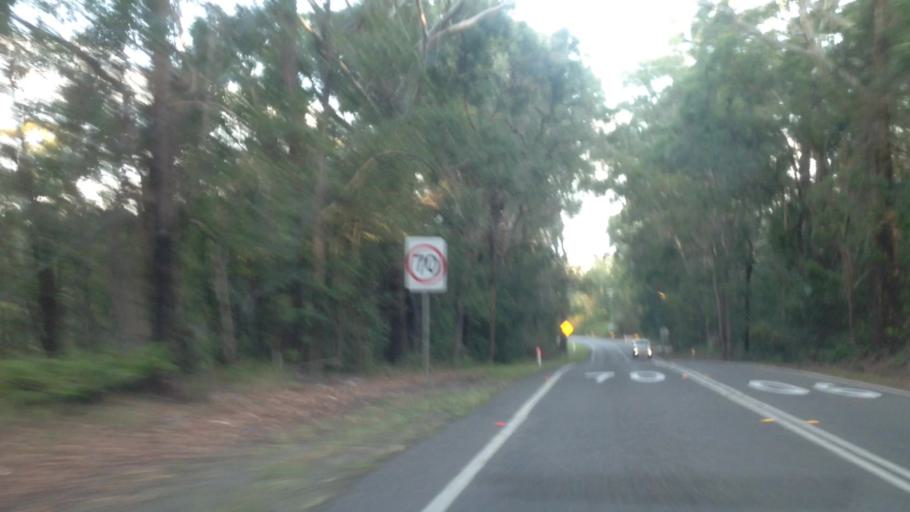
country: AU
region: New South Wales
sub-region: Lake Macquarie Shire
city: Cooranbong
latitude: -32.9796
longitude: 151.4839
